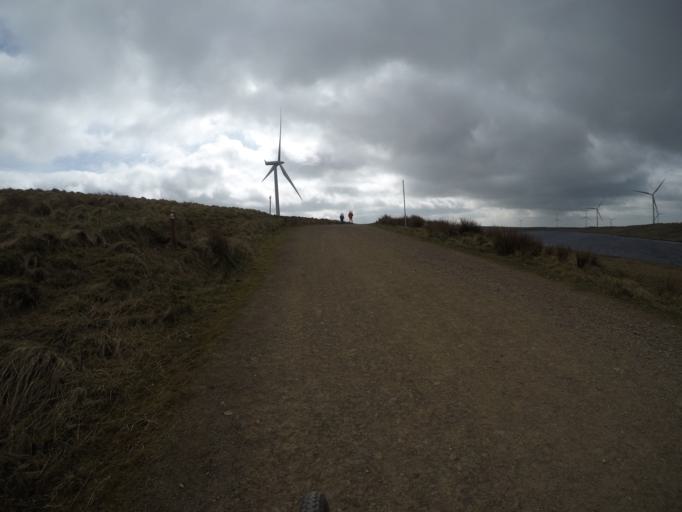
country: GB
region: Scotland
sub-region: East Renfrewshire
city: Eaglesham
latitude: 55.7051
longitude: -4.3238
